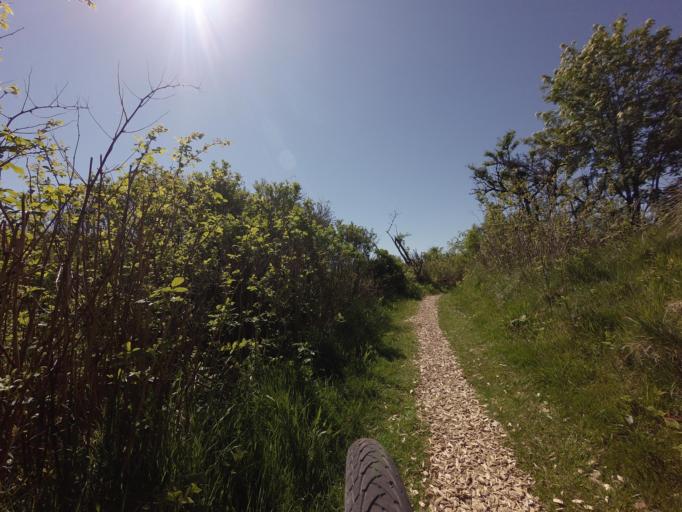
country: DK
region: North Denmark
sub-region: Jammerbugt Kommune
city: Pandrup
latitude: 57.2636
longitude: 9.6205
